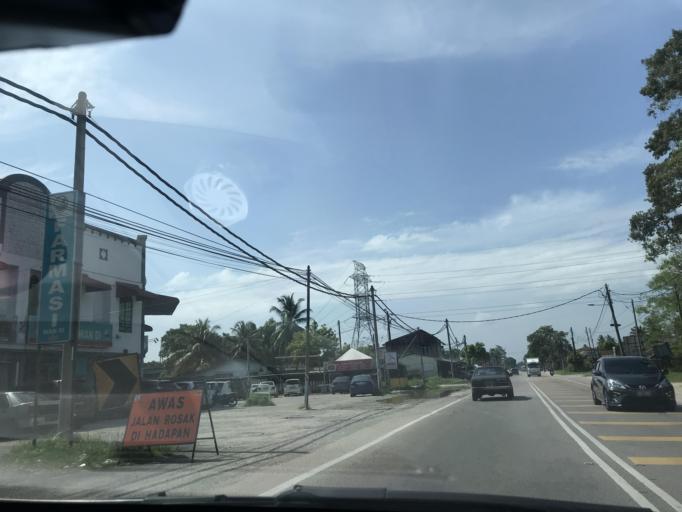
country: MY
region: Kelantan
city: Tumpat
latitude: 6.1490
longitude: 102.1617
